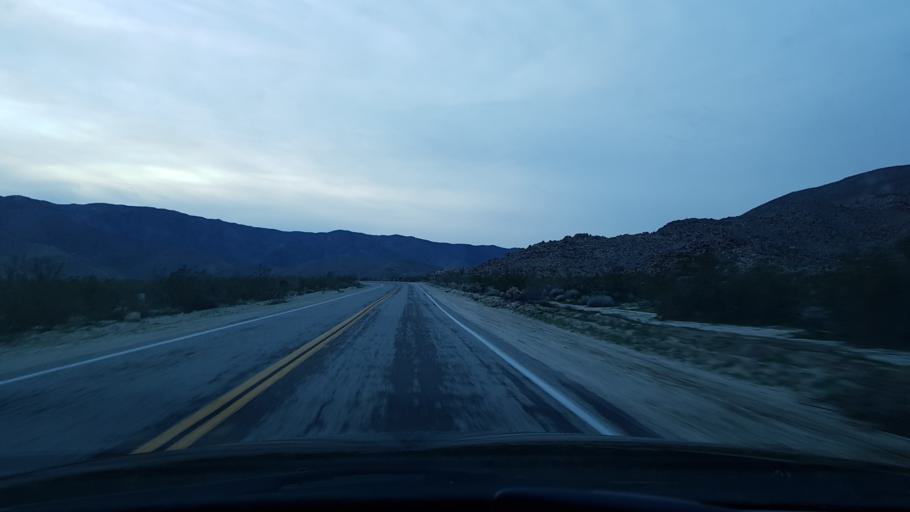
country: US
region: California
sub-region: San Diego County
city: Pine Valley
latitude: 32.9759
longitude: -116.3743
